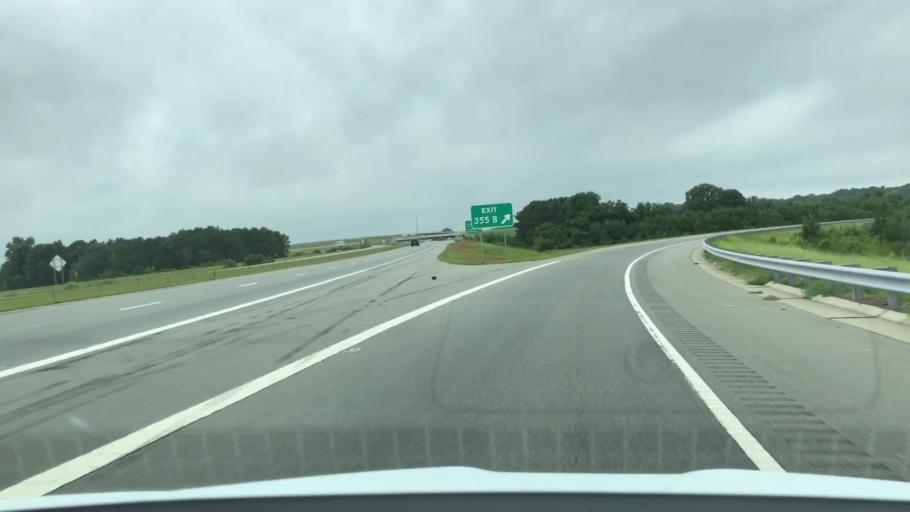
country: US
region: North Carolina
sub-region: Wayne County
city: Goldsboro
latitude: 35.4267
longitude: -77.9872
